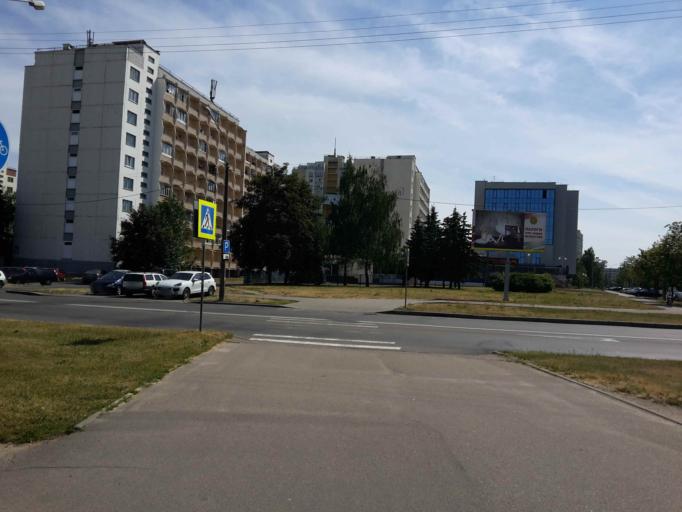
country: BY
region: Minsk
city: Minsk
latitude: 53.9282
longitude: 27.5659
